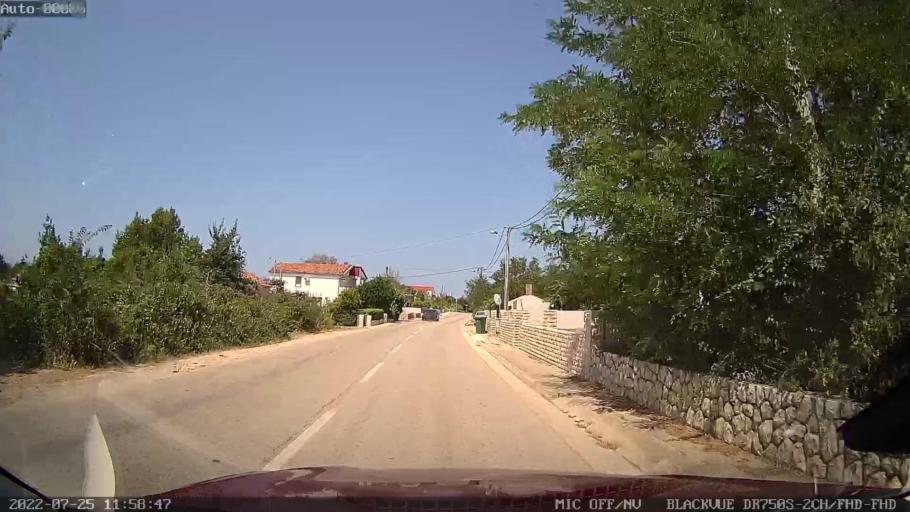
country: HR
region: Zadarska
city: Nin
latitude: 44.2393
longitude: 15.2087
